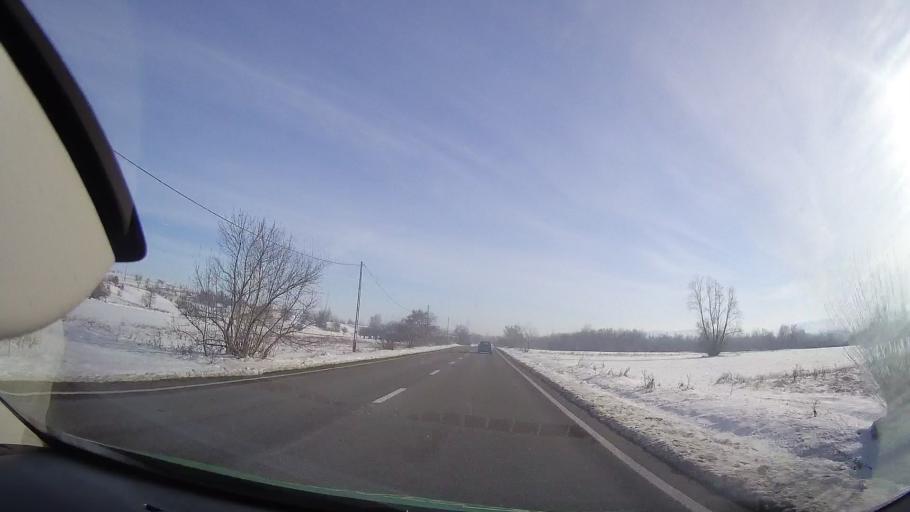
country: RO
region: Neamt
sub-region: Comuna Ghindaoani
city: Ghindaoani
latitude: 47.0770
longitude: 26.3518
